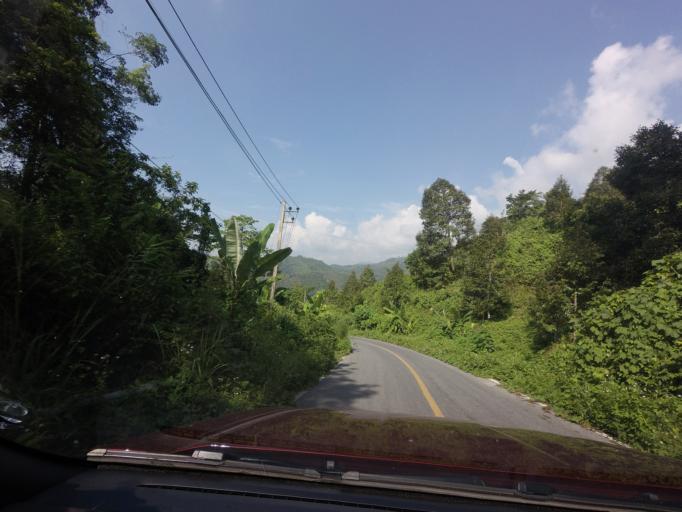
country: TH
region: Yala
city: Than To
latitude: 5.9903
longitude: 101.2032
